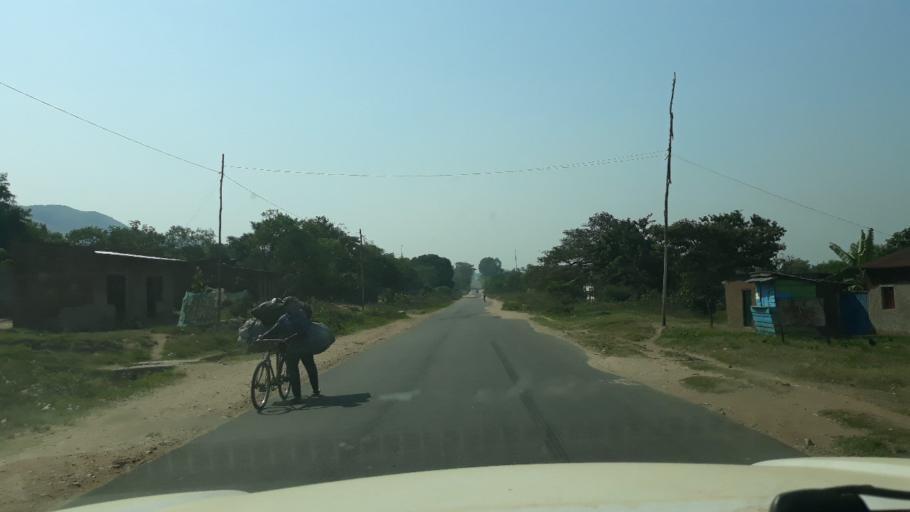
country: CD
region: South Kivu
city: Uvira
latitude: -3.2273
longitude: 29.1659
